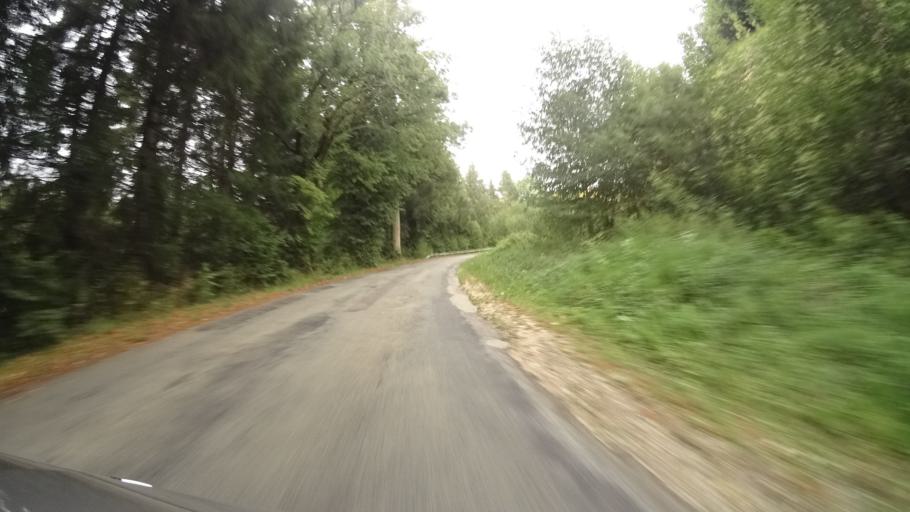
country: FR
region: Franche-Comte
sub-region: Departement du Jura
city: Morbier
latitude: 46.6578
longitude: 6.0779
